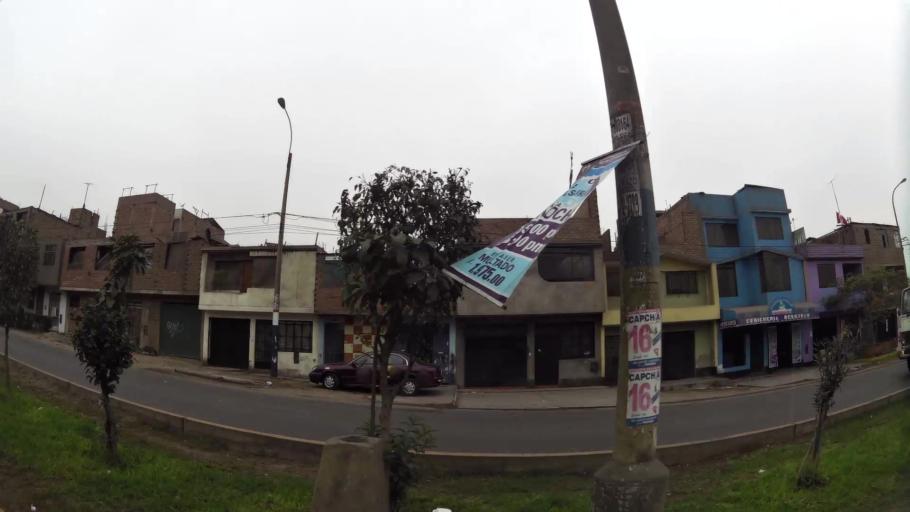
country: PE
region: Lima
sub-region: Lima
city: Independencia
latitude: -11.9587
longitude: -76.9841
